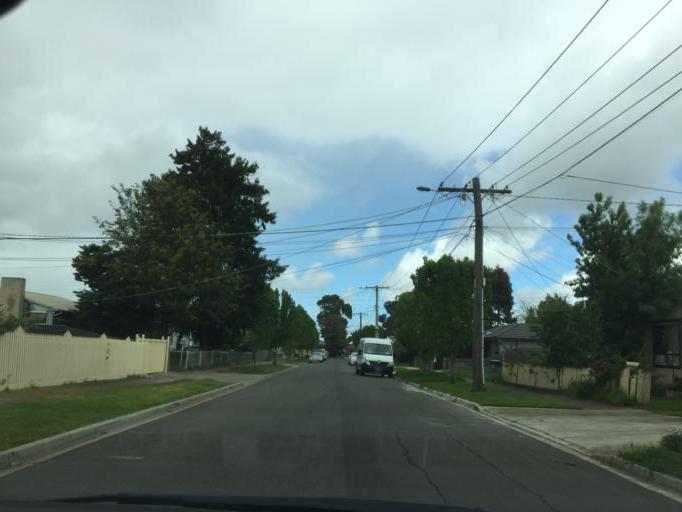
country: AU
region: Victoria
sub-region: Brimbank
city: Sunshine North
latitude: -37.7808
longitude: 144.8237
